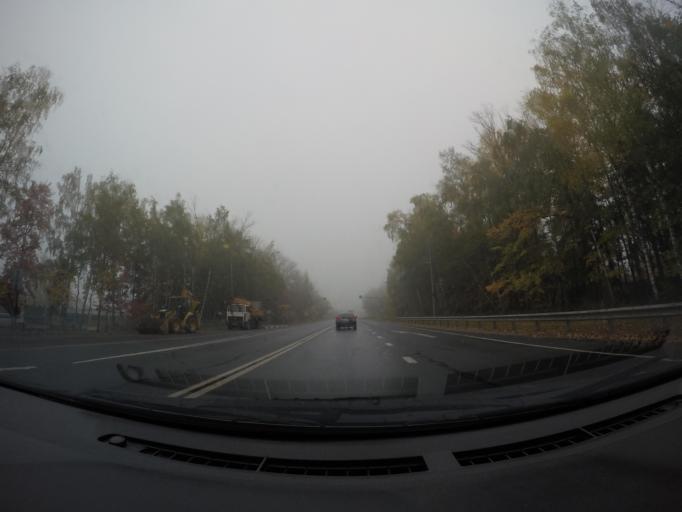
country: RU
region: Moskovskaya
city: Ruza
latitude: 55.7121
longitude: 36.2056
